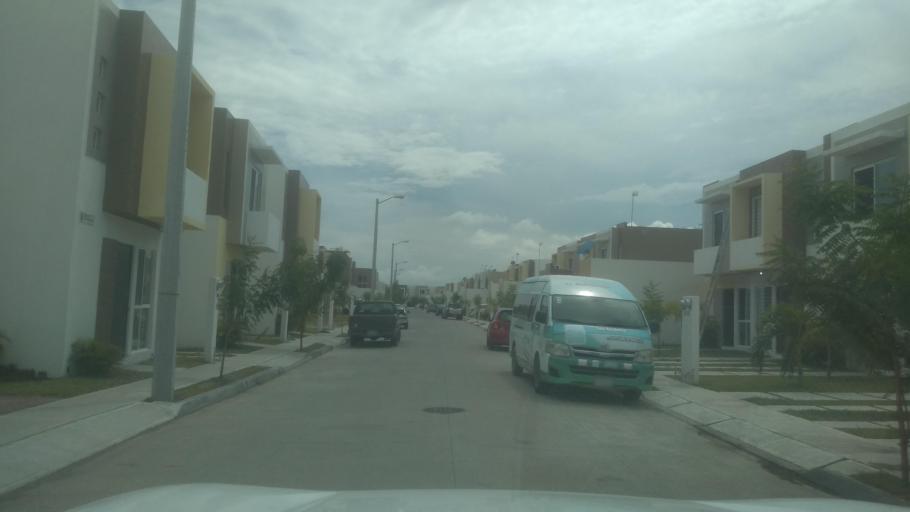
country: MX
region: Veracruz
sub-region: Medellin
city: Fraccionamiento Arboledas San Ramon
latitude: 19.1056
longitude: -96.1651
